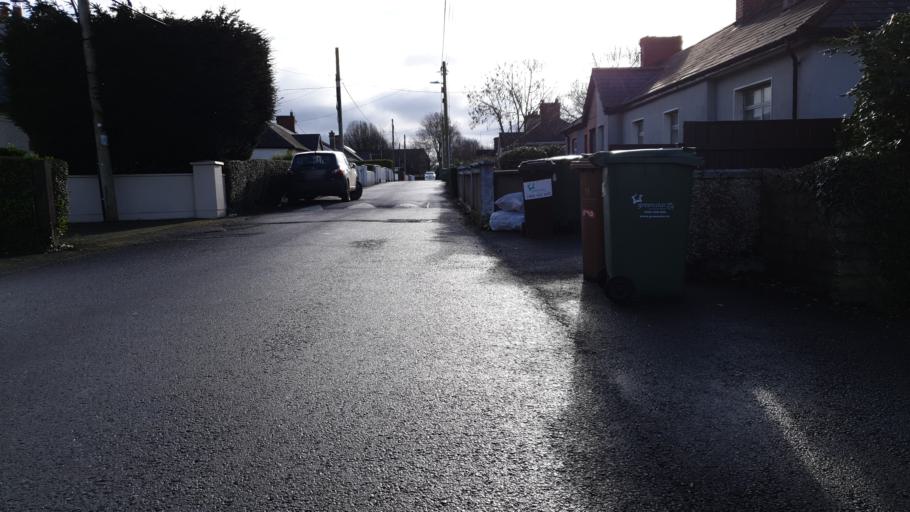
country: IE
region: Munster
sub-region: County Cork
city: Passage West
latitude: 51.8958
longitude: -8.4056
